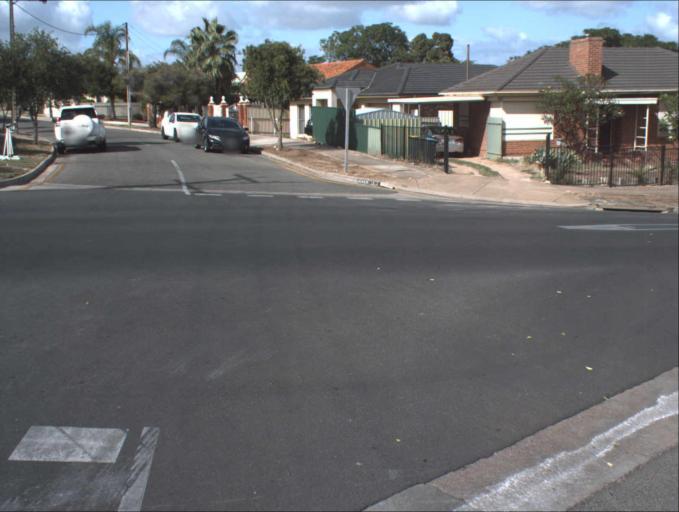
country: AU
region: South Australia
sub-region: Port Adelaide Enfield
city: Blair Athol
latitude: -34.8616
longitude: 138.5954
